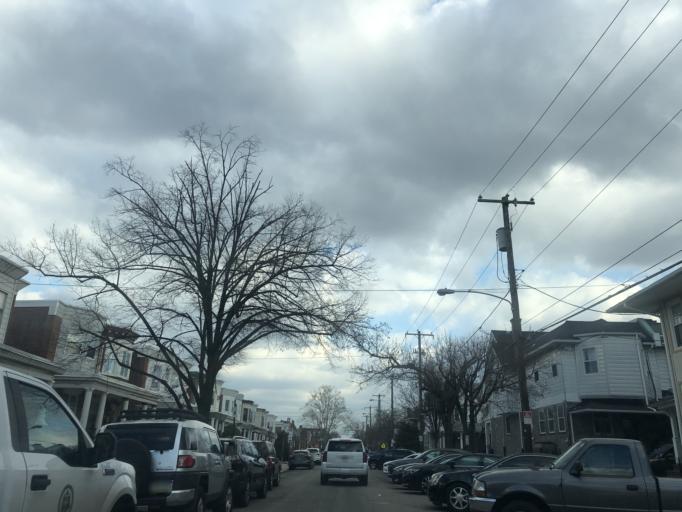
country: US
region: Pennsylvania
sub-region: Philadelphia County
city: Philadelphia
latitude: 39.9205
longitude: -75.1787
